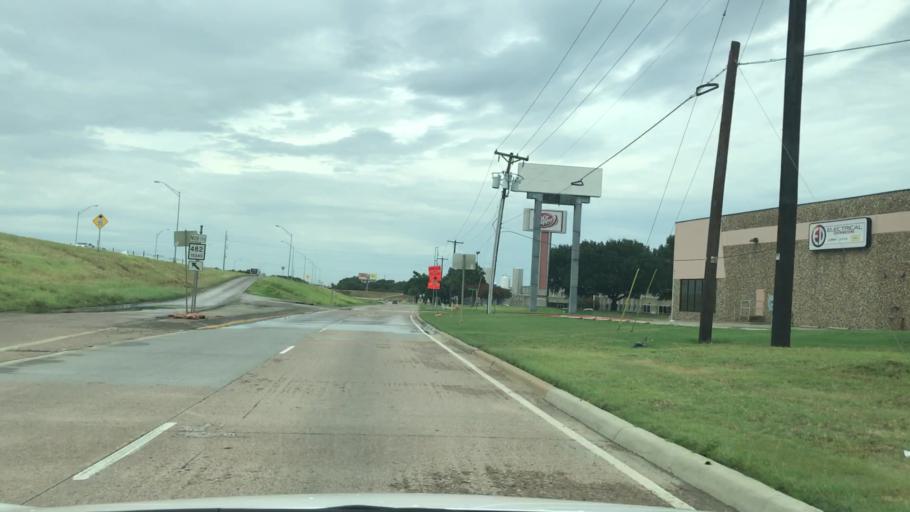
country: US
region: Texas
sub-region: Dallas County
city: Irving
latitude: 32.8428
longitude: -96.8995
